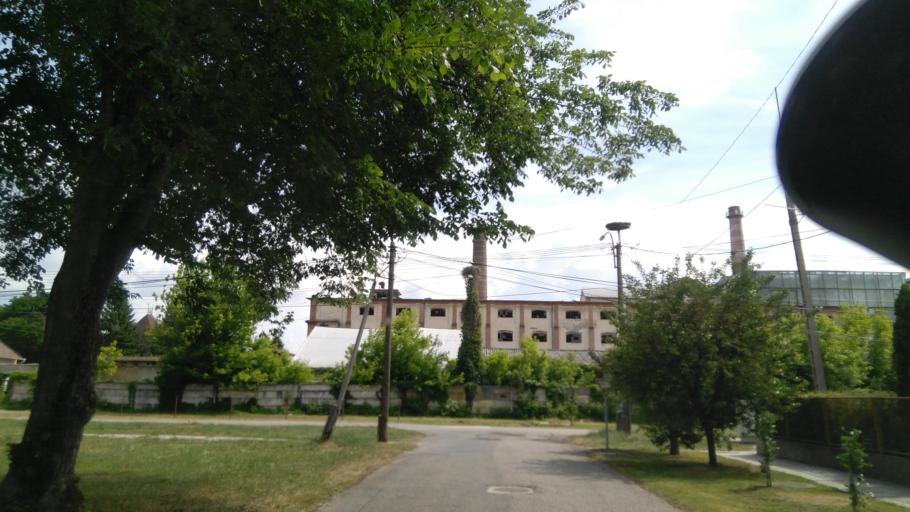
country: HU
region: Bekes
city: Mezohegyes
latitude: 46.3110
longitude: 20.8089
